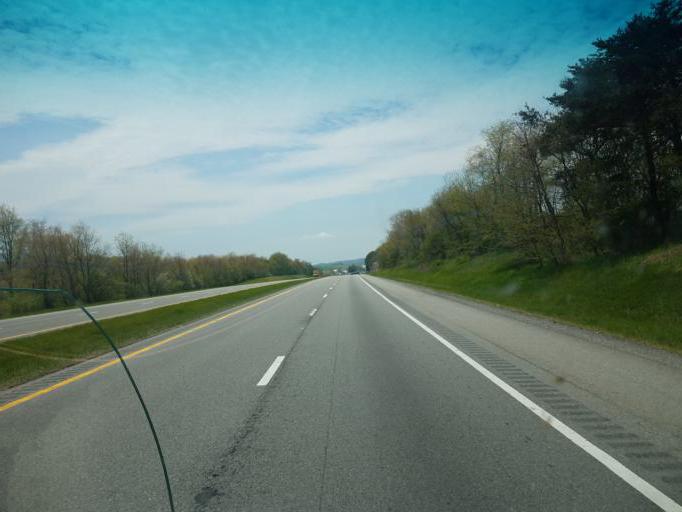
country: US
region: Virginia
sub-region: Wythe County
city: Rural Retreat
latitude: 36.9027
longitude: -81.3187
